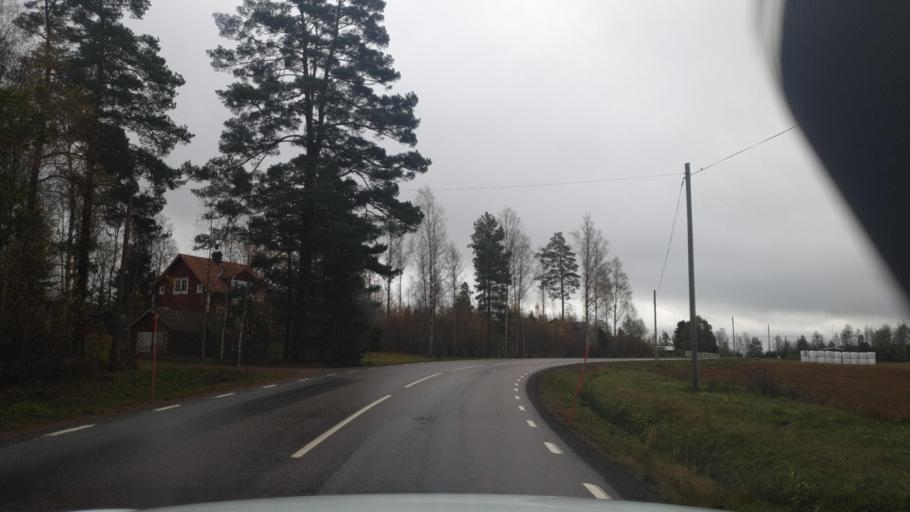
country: SE
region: Vaermland
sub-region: Eda Kommun
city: Amotfors
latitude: 59.7809
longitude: 12.2656
